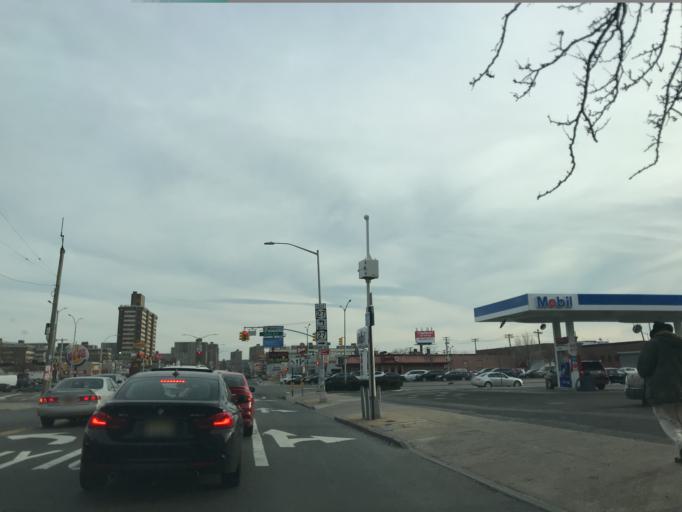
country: US
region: New York
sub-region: Kings County
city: East New York
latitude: 40.6592
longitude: -73.8911
